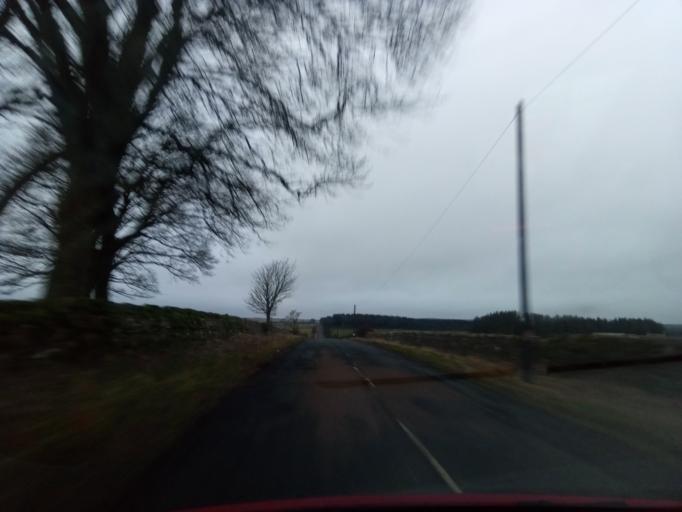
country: GB
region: England
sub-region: Northumberland
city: Rothley
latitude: 55.1993
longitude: -1.9760
